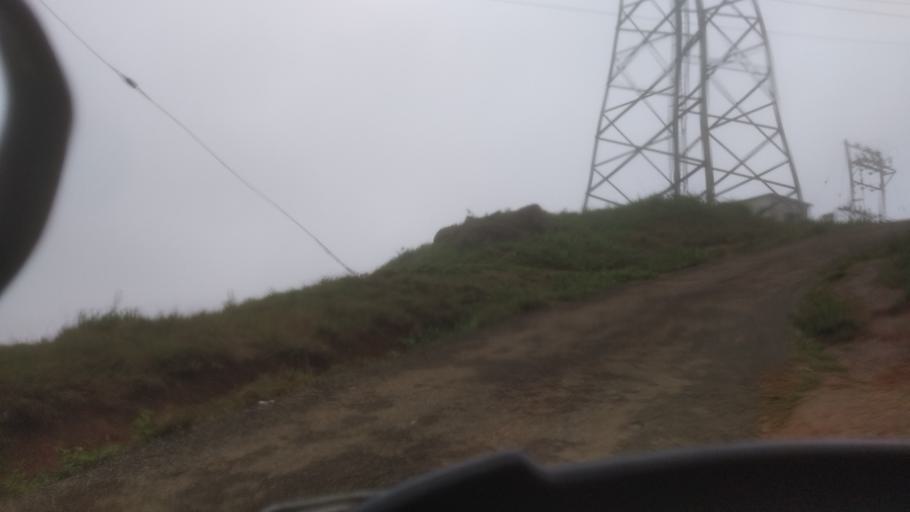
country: IN
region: Tamil Nadu
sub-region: Theni
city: Kombai
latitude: 9.8858
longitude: 77.2212
